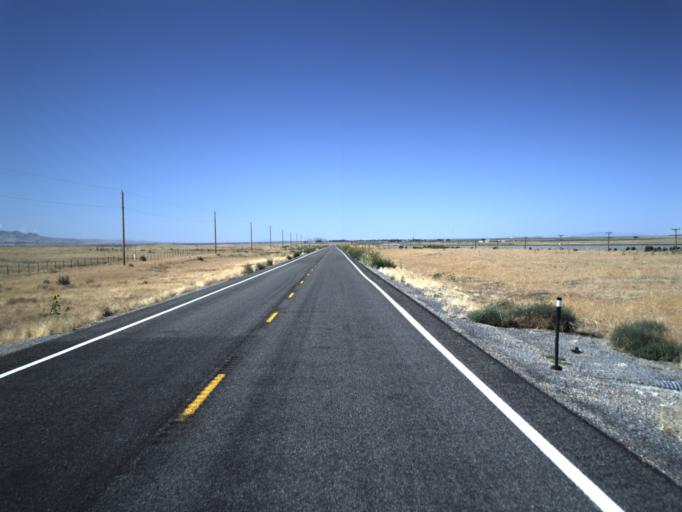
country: US
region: Utah
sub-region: Millard County
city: Delta
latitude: 39.6026
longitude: -112.3240
